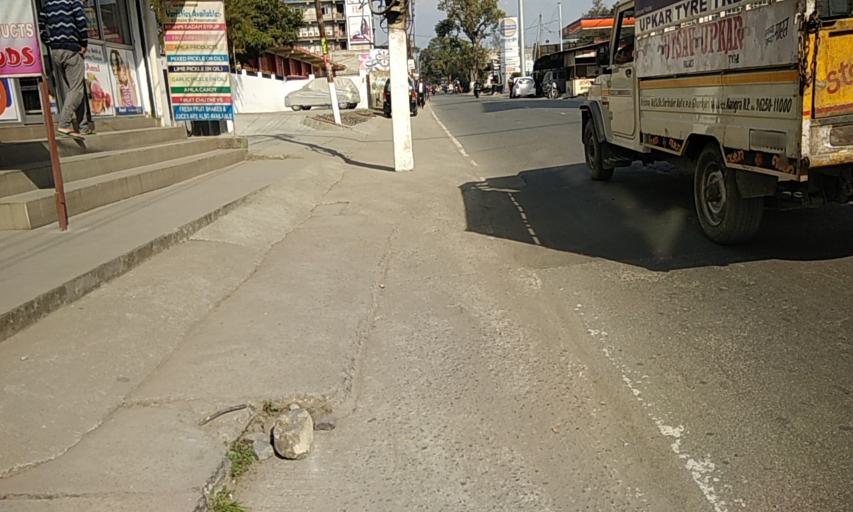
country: IN
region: Himachal Pradesh
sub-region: Kangra
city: Kangra
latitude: 32.1142
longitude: 76.2813
